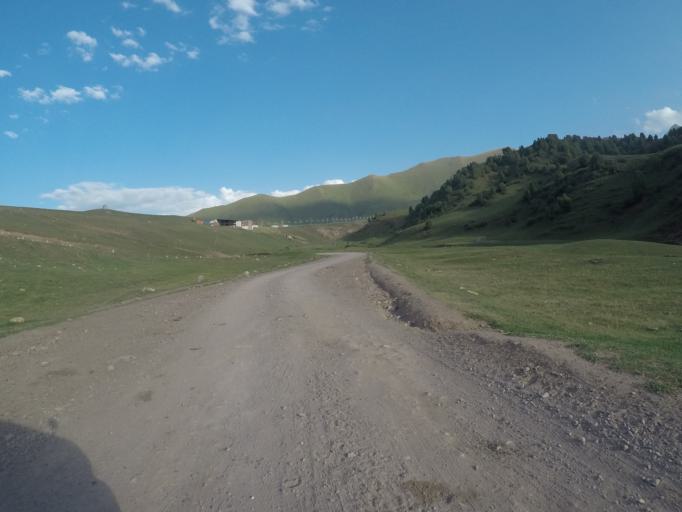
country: KG
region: Chuy
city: Bishkek
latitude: 42.6410
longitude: 74.6242
